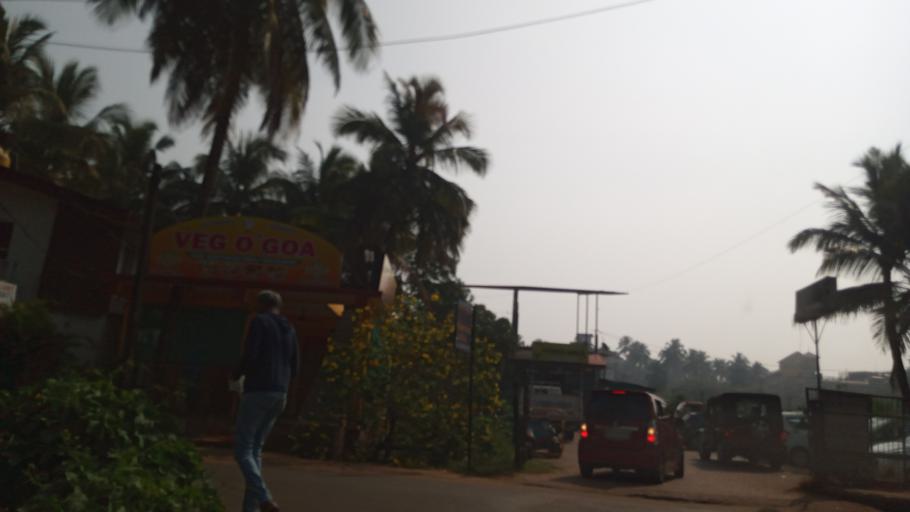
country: IN
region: Goa
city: Calangute
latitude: 15.5415
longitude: 73.7608
